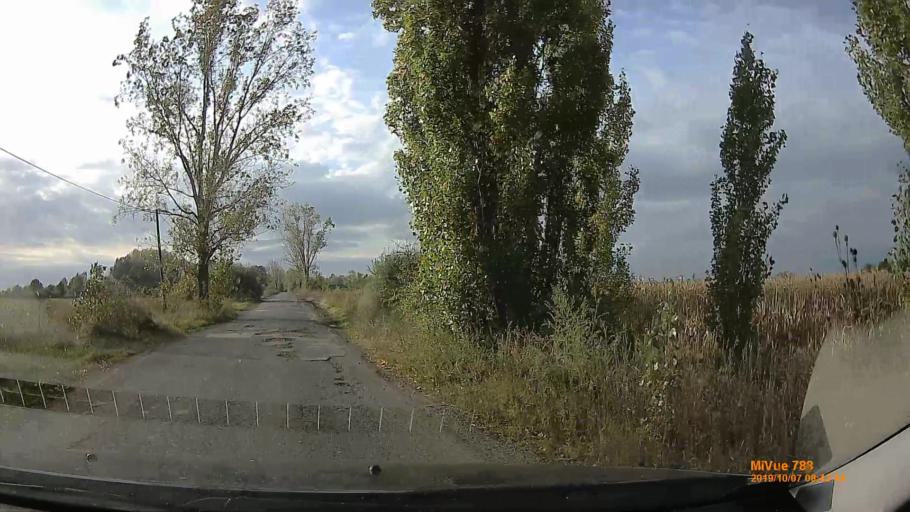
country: HU
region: Bekes
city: Szarvas
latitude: 46.8151
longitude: 20.5261
